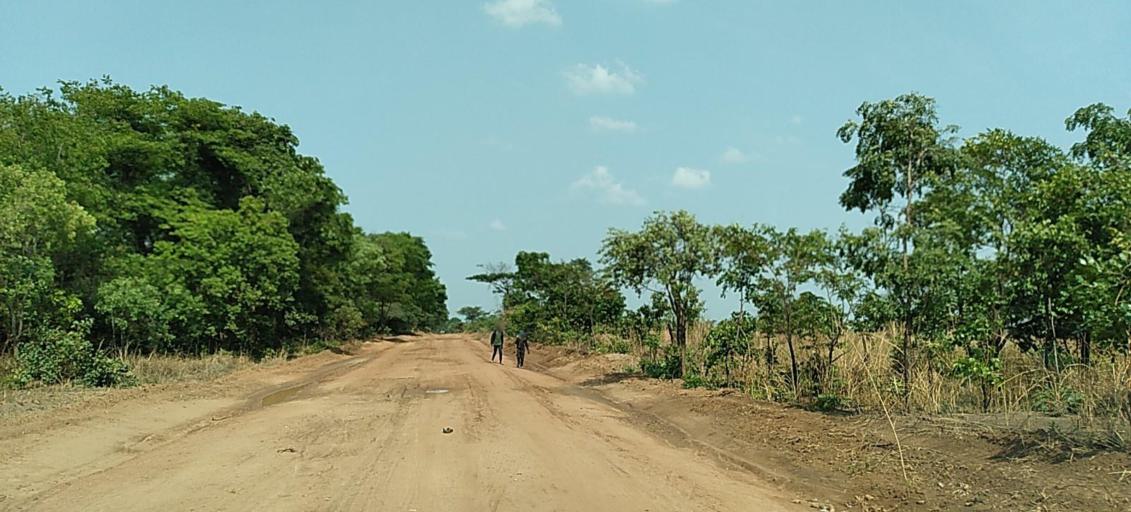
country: ZM
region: Copperbelt
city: Luanshya
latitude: -13.0907
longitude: 28.2808
